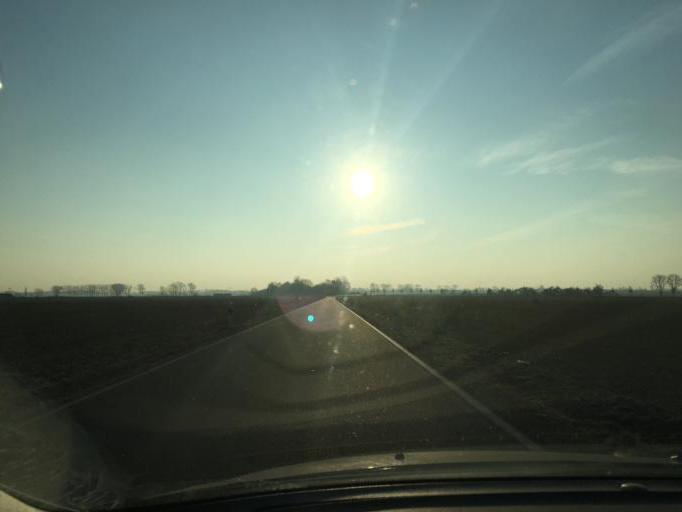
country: DE
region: Saxony
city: Borsdorf
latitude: 51.3310
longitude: 12.5041
